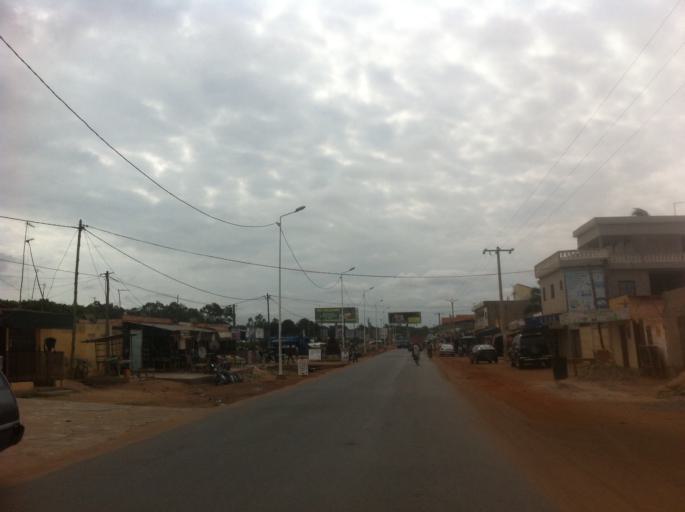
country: TG
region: Maritime
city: Lome
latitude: 6.1887
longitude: 1.1598
